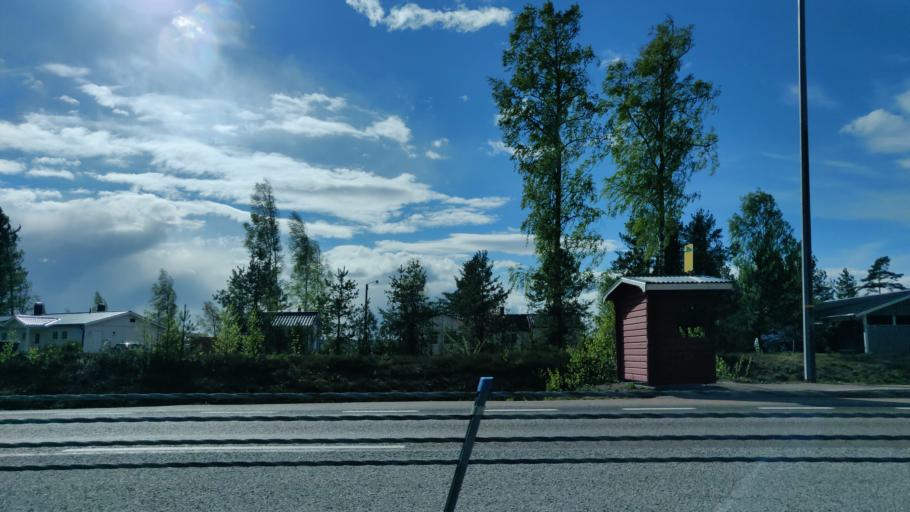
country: SE
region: Vaermland
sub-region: Forshaga Kommun
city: Forshaga
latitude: 59.4766
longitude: 13.4106
